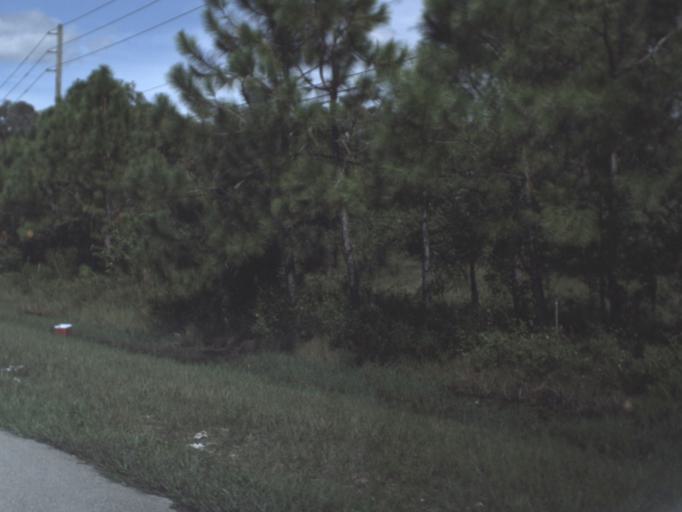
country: US
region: Florida
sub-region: Lee County
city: Pine Manor
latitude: 26.5887
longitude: -81.8532
